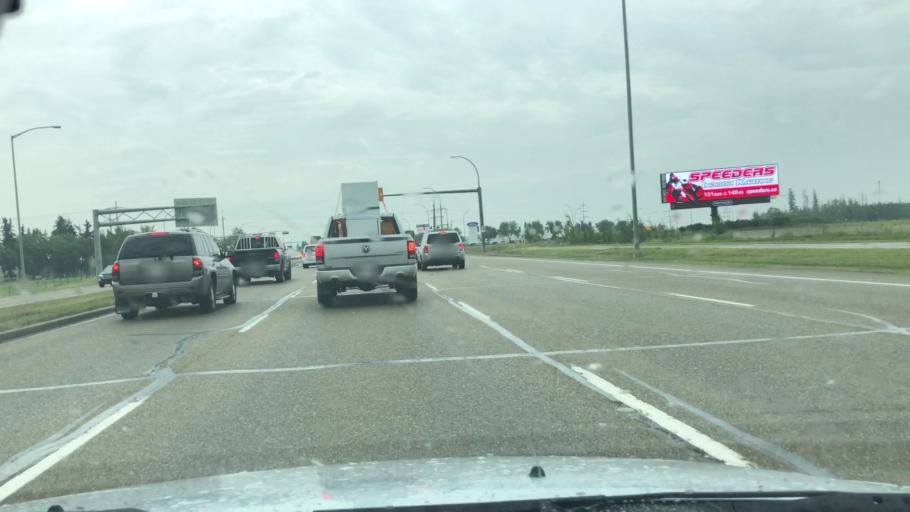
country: CA
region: Alberta
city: St. Albert
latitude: 53.6129
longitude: -113.5936
